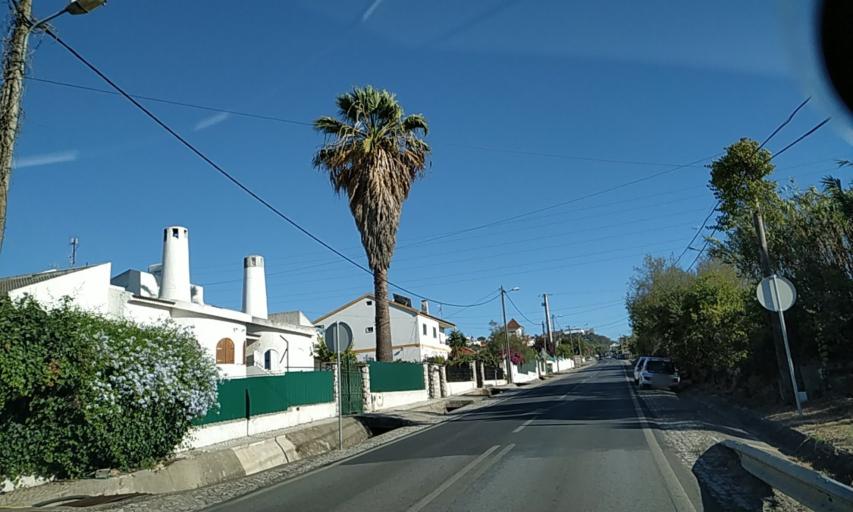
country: PT
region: Setubal
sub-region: Palmela
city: Palmela
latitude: 38.5812
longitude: -8.9094
